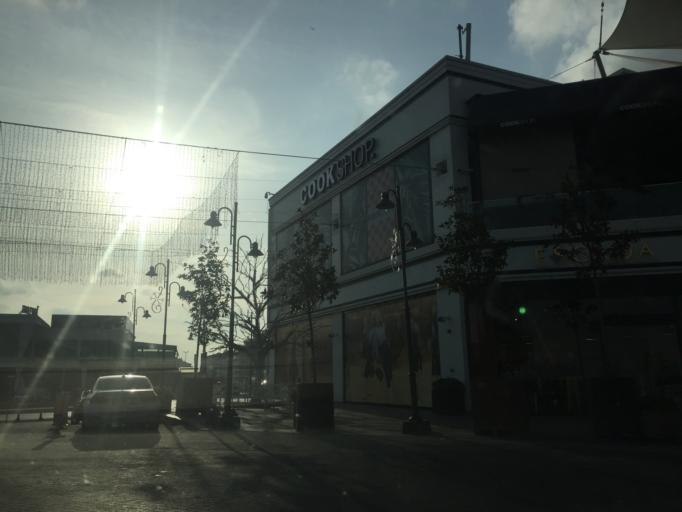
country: TR
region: Istanbul
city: Sultanbeyli
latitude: 40.9356
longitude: 29.3283
